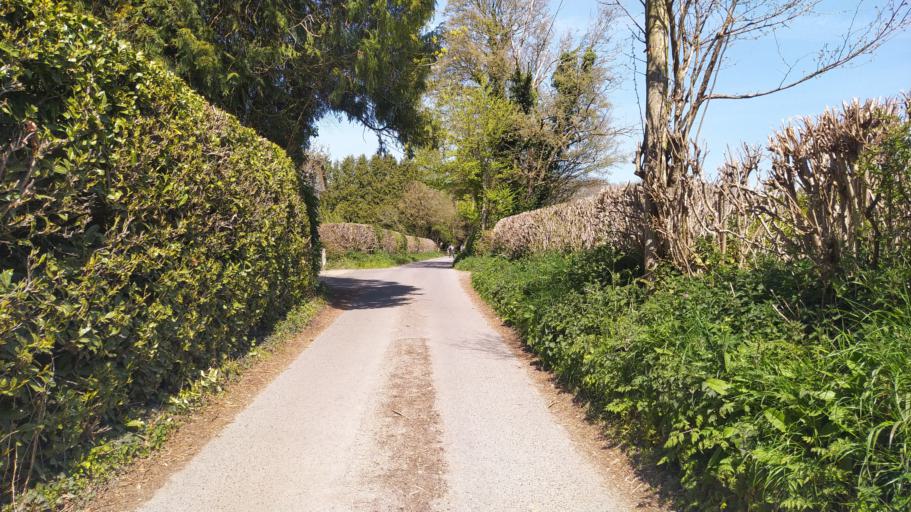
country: GB
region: England
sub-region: Dorset
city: Manston
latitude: 50.9094
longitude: -2.2453
